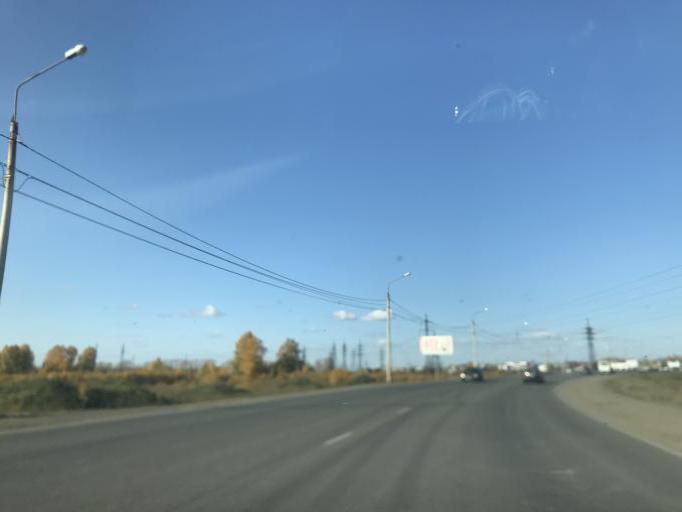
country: RU
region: Chelyabinsk
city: Roshchino
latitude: 55.2266
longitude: 61.2876
